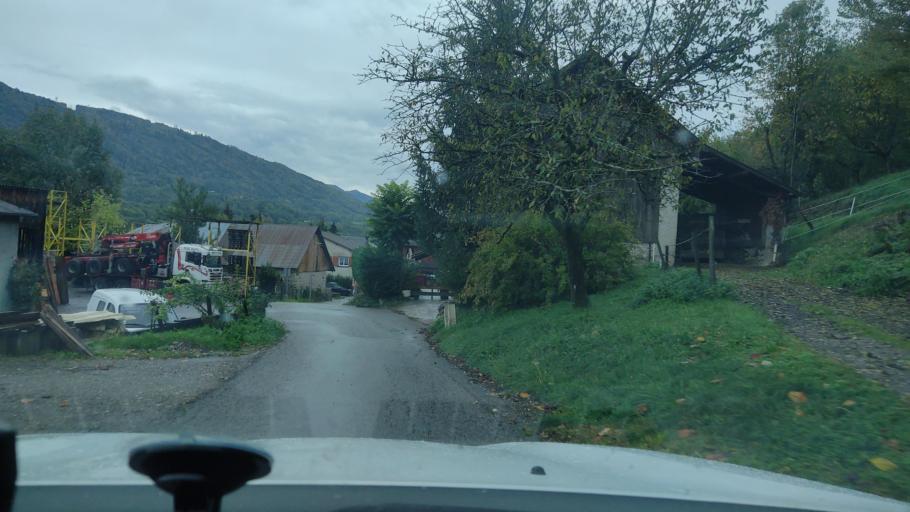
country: FR
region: Rhone-Alpes
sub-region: Departement de la Savoie
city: Cruet
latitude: 45.5011
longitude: 6.1017
